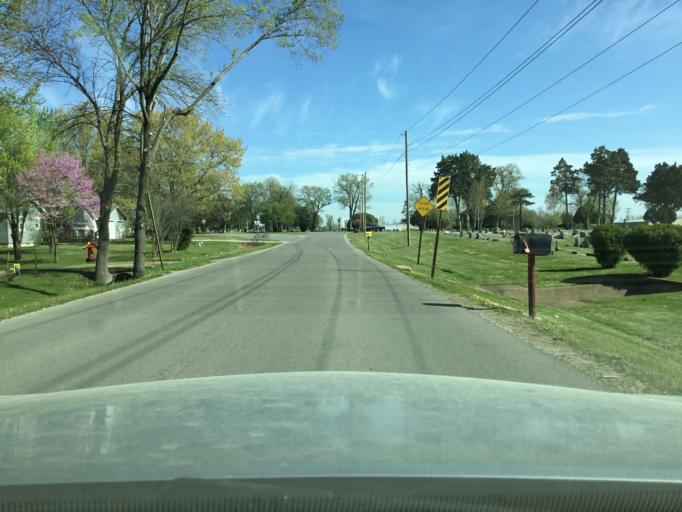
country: US
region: Kansas
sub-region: Neosho County
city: Chanute
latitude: 37.6662
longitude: -95.4434
